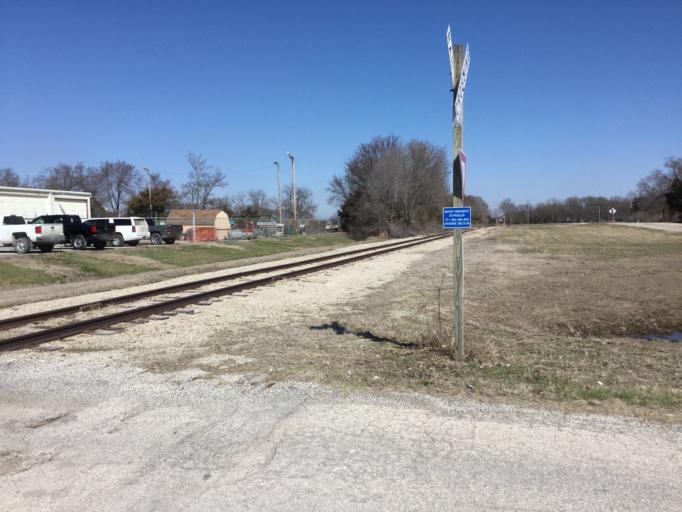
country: US
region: Kansas
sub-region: Allen County
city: Humboldt
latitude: 37.8167
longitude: -95.4285
